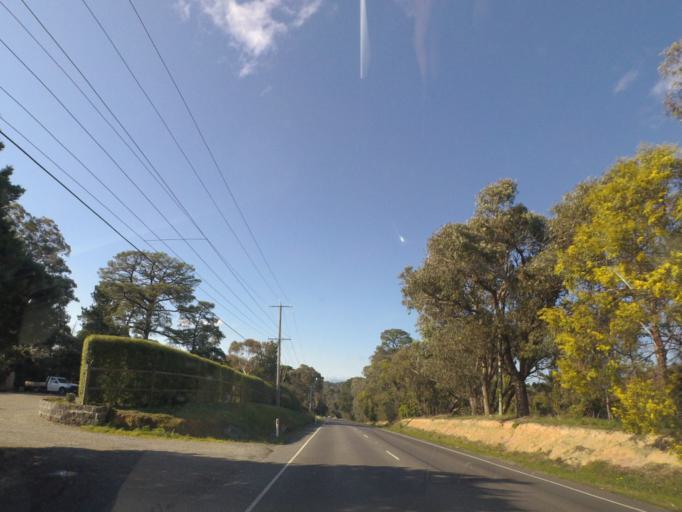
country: AU
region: Victoria
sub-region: Manningham
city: Park Orchards
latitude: -37.7702
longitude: 145.2228
